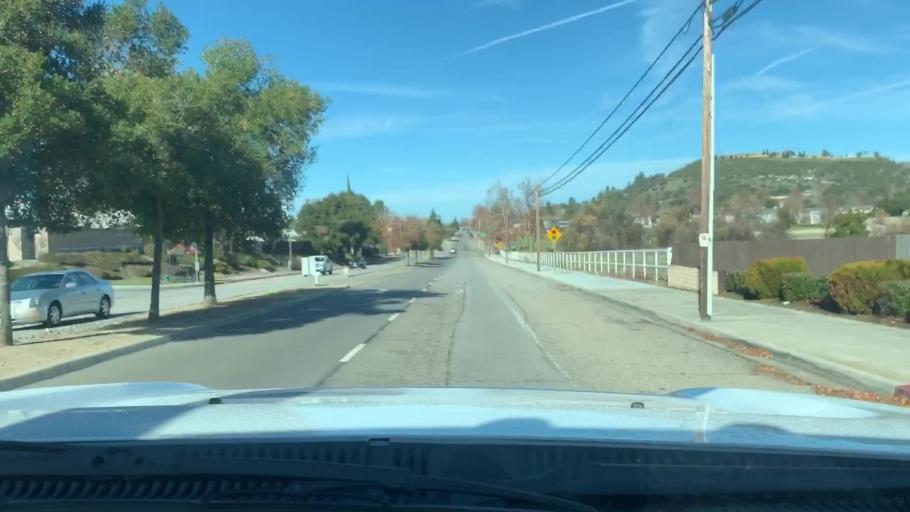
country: US
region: California
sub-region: San Luis Obispo County
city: Atascadero
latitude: 35.4584
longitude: -120.6421
